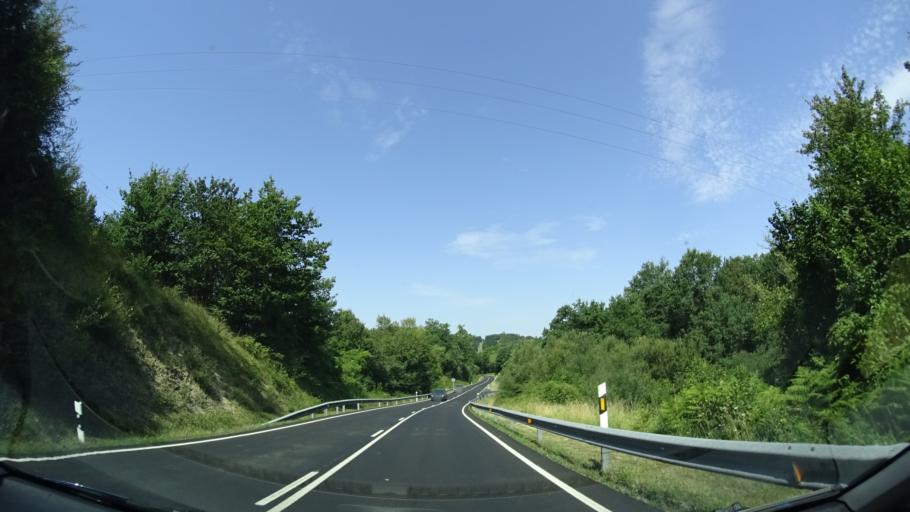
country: ES
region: Basque Country
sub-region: Provincia de Alava
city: Murguia
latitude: 42.9638
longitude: -2.8954
